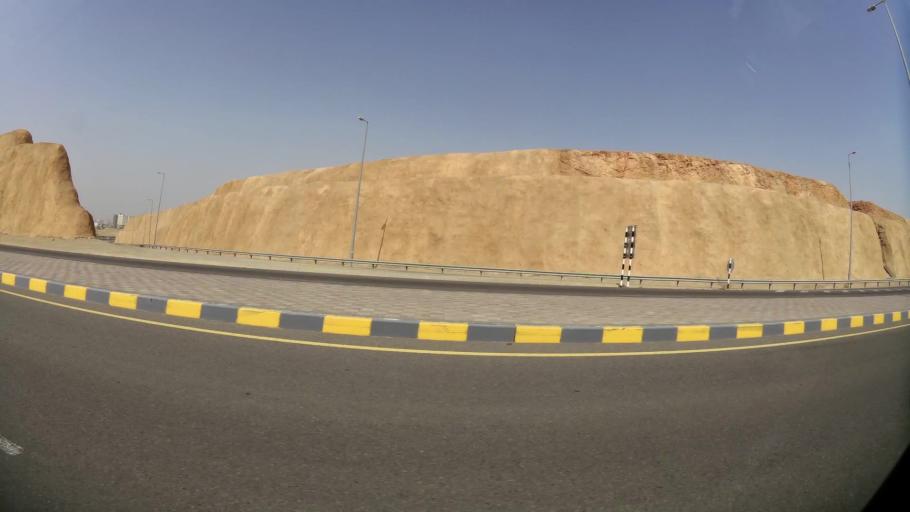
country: OM
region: Muhafazat Masqat
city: Bawshar
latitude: 23.5582
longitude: 58.3393
